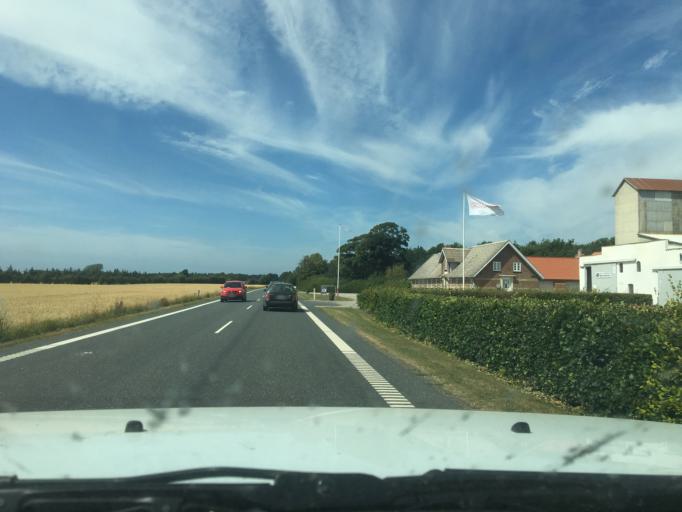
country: DK
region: Central Jutland
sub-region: Viborg Kommune
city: Viborg
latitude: 56.5943
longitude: 9.3641
